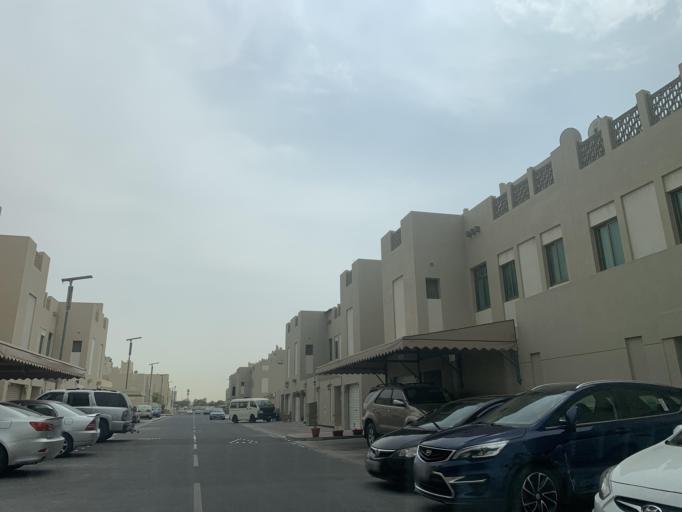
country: BH
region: Northern
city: Madinat `Isa
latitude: 26.1704
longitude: 50.5109
